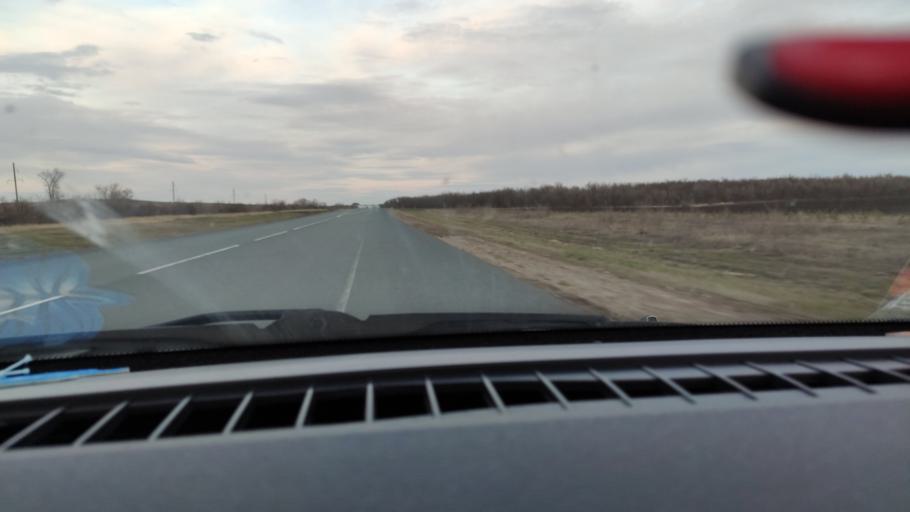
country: RU
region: Saratov
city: Yelshanka
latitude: 51.8271
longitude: 46.2728
